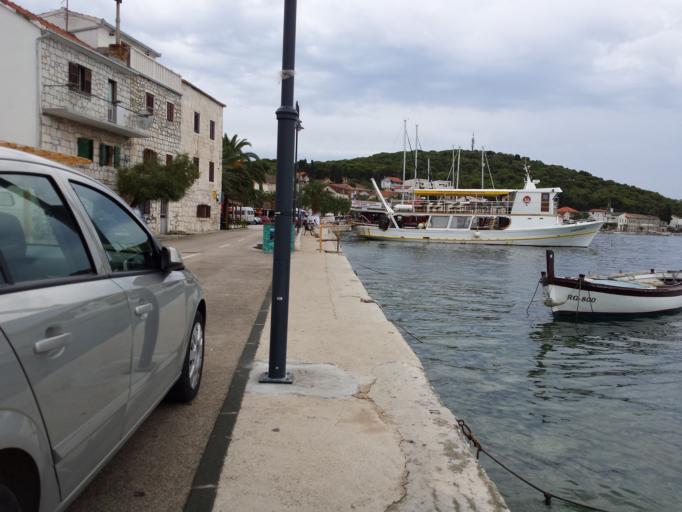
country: HR
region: Sibensko-Kniniska
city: Rogoznica
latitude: 43.5275
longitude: 15.9684
